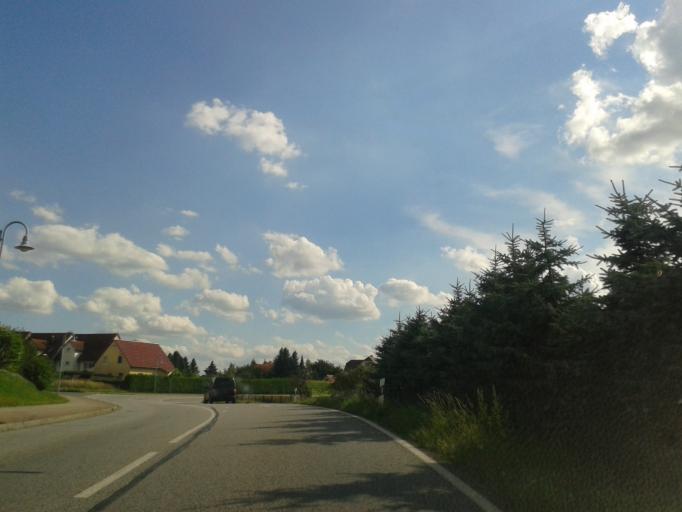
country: DE
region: Saxony
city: Lichtenberg
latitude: 51.1531
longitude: 13.9644
